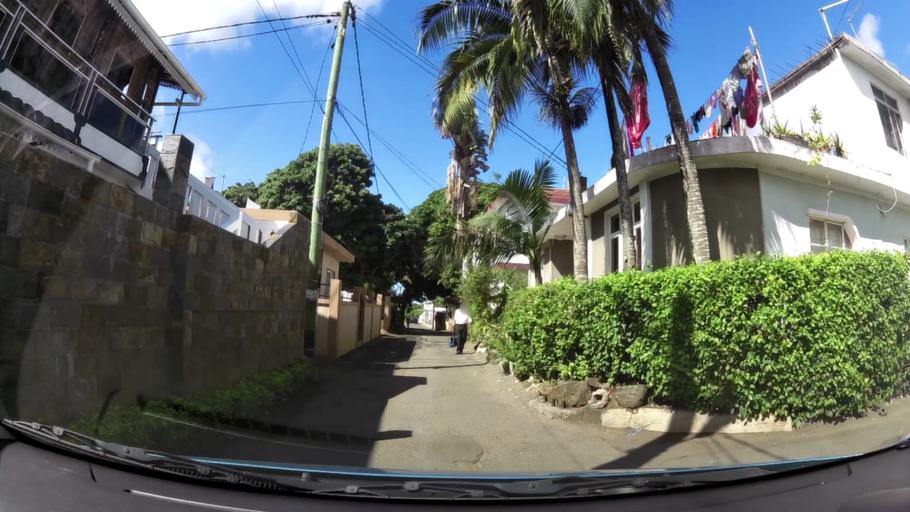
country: MU
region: Grand Port
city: Plaine Magnien
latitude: -20.4283
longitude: 57.6586
